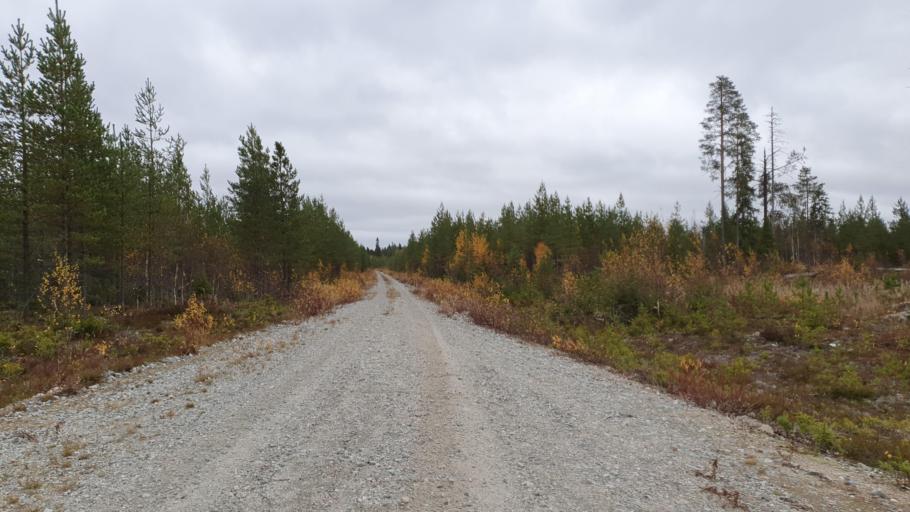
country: FI
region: Kainuu
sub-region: Kehys-Kainuu
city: Kuhmo
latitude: 64.4480
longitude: 29.6017
